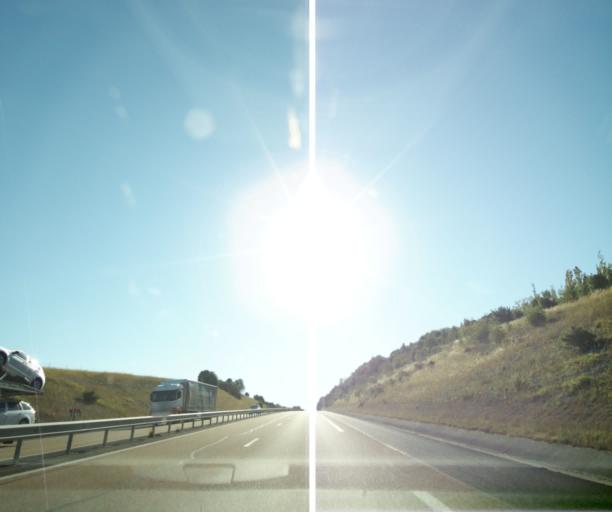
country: FR
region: Champagne-Ardenne
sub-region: Departement de l'Aube
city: Aix-en-Othe
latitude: 48.2581
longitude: 3.6427
